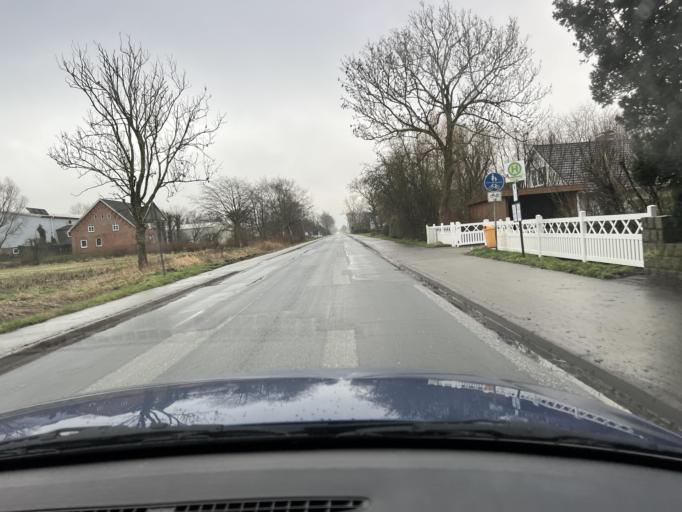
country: DE
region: Schleswig-Holstein
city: Norderwohrden
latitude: 54.2188
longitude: 9.0220
